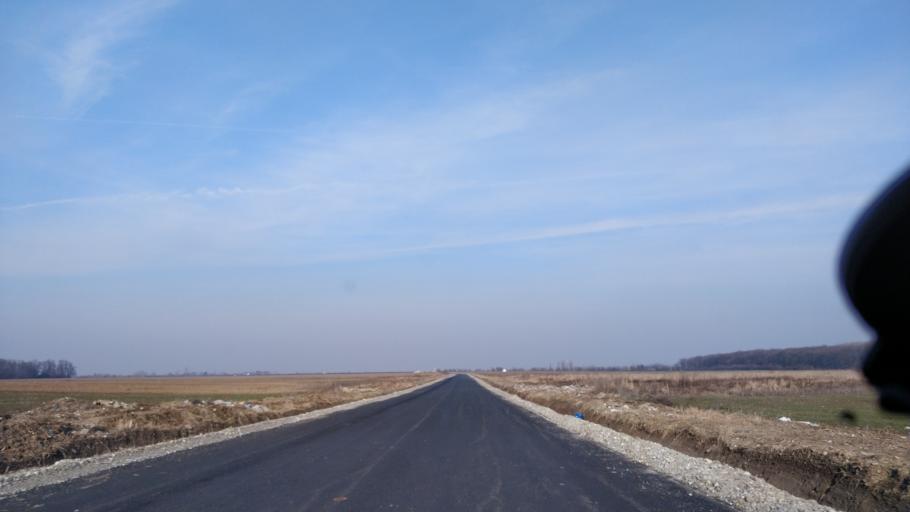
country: RO
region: Dambovita
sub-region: Comuna Brezoaiele
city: Brezoaia
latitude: 44.5279
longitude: 25.7861
